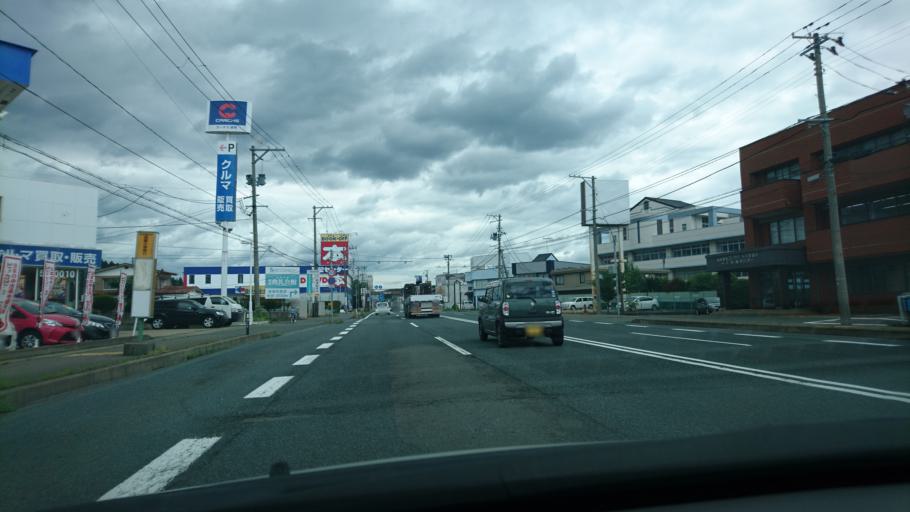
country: JP
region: Iwate
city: Morioka-shi
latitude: 39.6901
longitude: 141.1655
